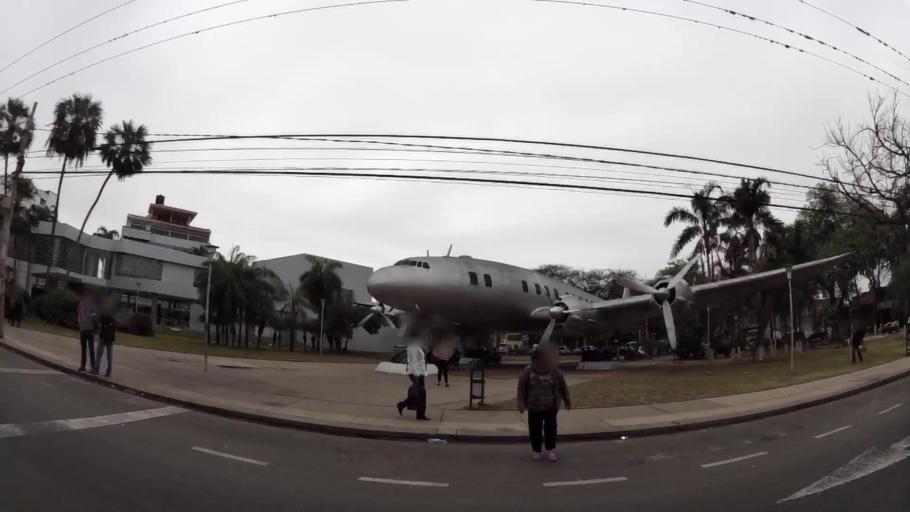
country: BO
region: Santa Cruz
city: Santa Cruz de la Sierra
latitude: -17.7757
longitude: -63.1743
